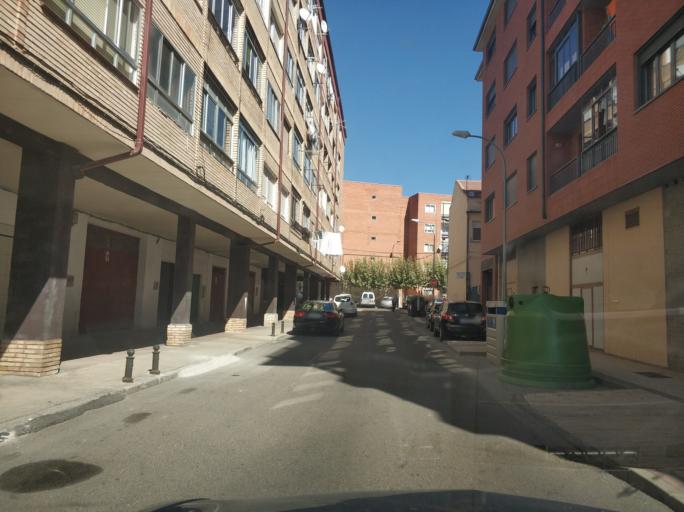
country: ES
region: Castille and Leon
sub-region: Provincia de Burgos
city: Aranda de Duero
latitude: 41.6697
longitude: -3.6773
